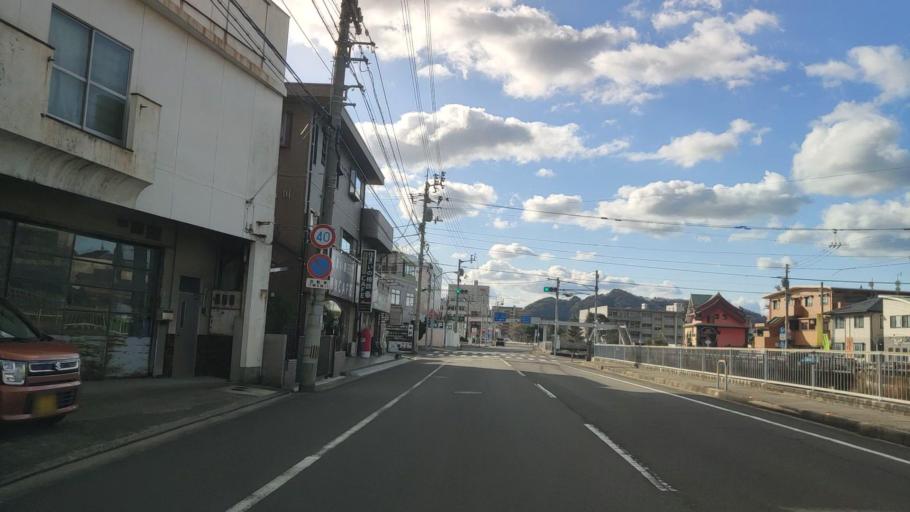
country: JP
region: Ehime
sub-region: Shikoku-chuo Shi
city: Matsuyama
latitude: 33.8592
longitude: 132.7193
